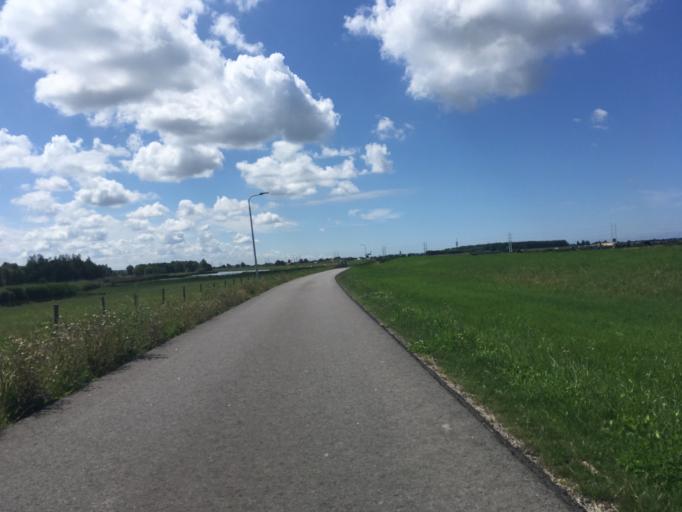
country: NL
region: North Holland
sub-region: Gemeente Velsen
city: Velsen-Zuid
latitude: 52.4139
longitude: 4.7257
